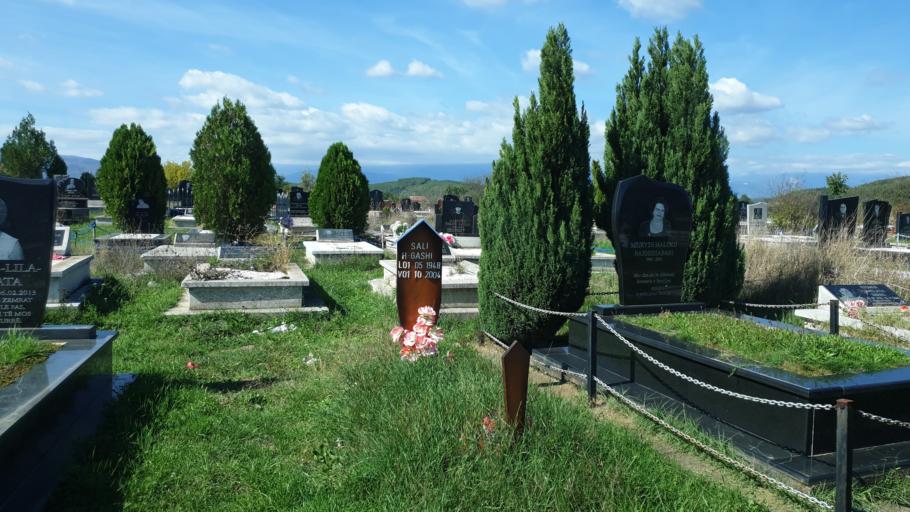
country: XK
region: Gjakova
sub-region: Komuna e Gjakoves
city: Gjakove
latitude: 42.3719
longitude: 20.4086
